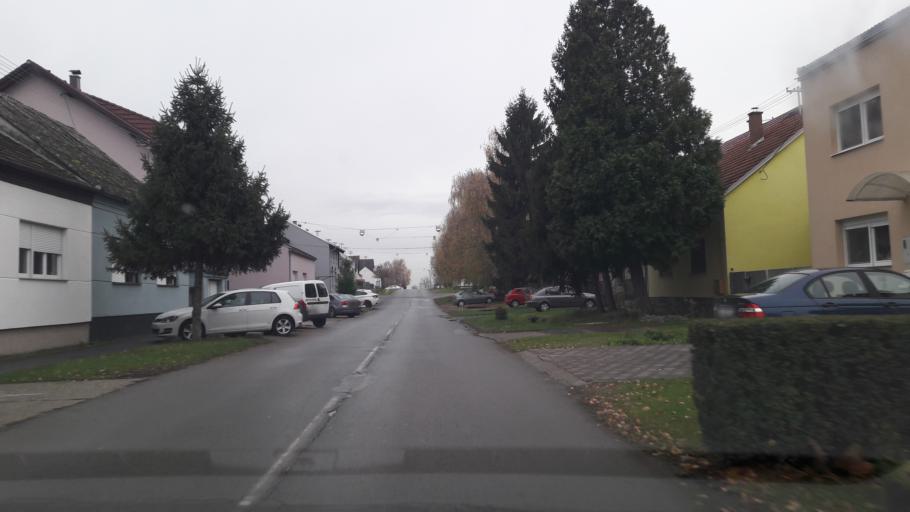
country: HR
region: Osjecko-Baranjska
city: Visnjevac
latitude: 45.5680
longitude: 18.6135
